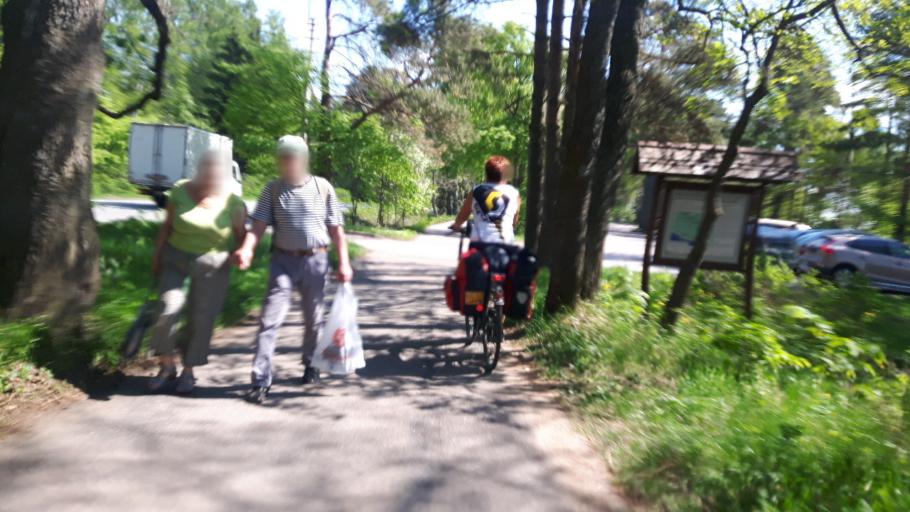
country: RU
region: St.-Petersburg
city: Komarovo
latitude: 60.1771
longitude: 29.7921
